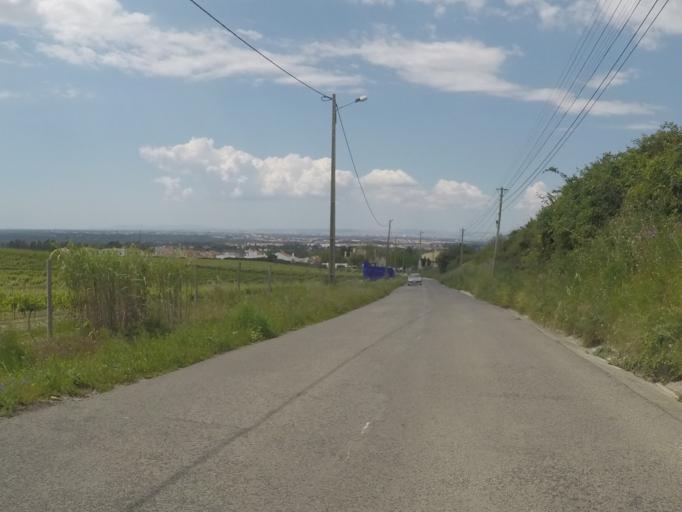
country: PT
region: Setubal
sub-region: Palmela
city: Quinta do Anjo
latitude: 38.5136
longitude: -9.0069
